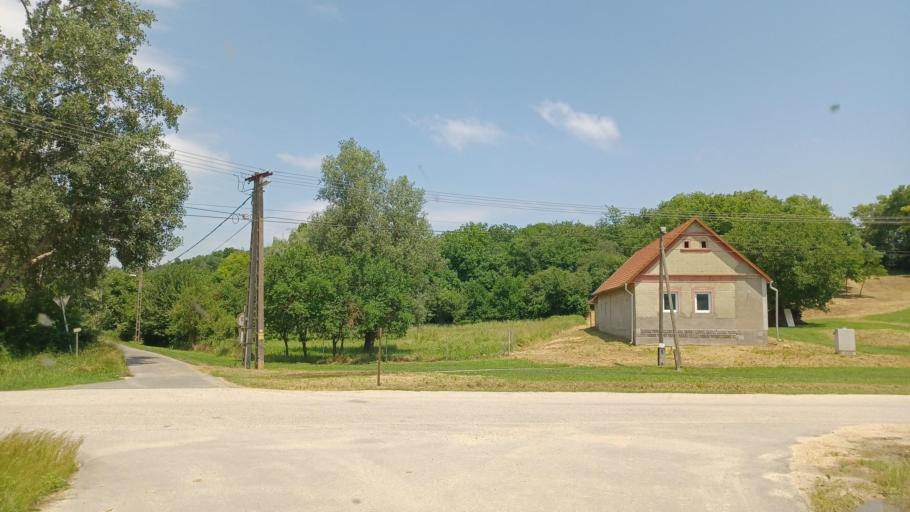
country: HU
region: Tolna
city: Simontornya
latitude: 46.6742
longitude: 18.5491
